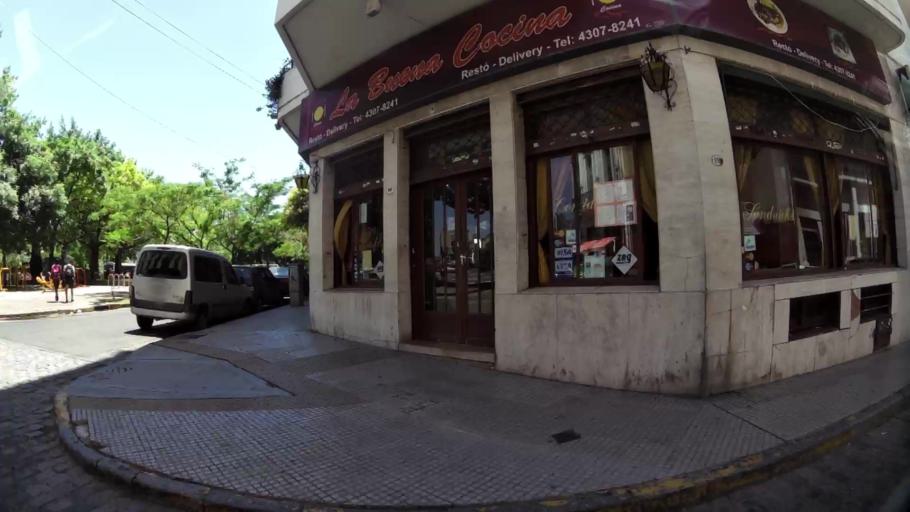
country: AR
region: Buenos Aires F.D.
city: Buenos Aires
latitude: -34.6185
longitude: -58.3797
